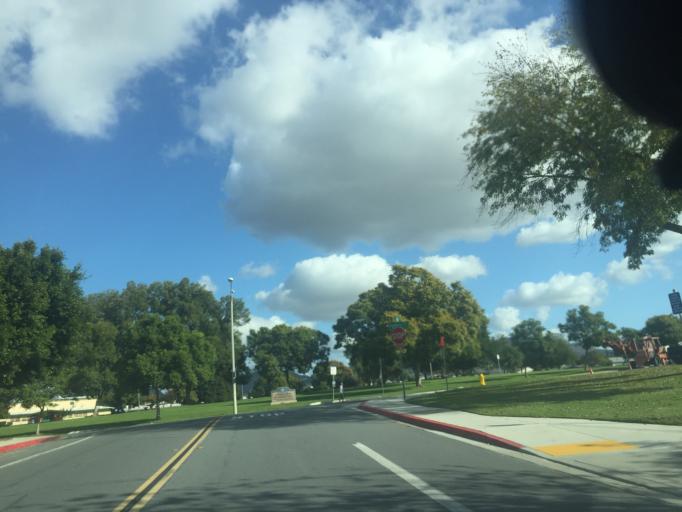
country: US
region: California
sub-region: San Diego County
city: La Mesa
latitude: 32.7943
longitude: -117.0815
